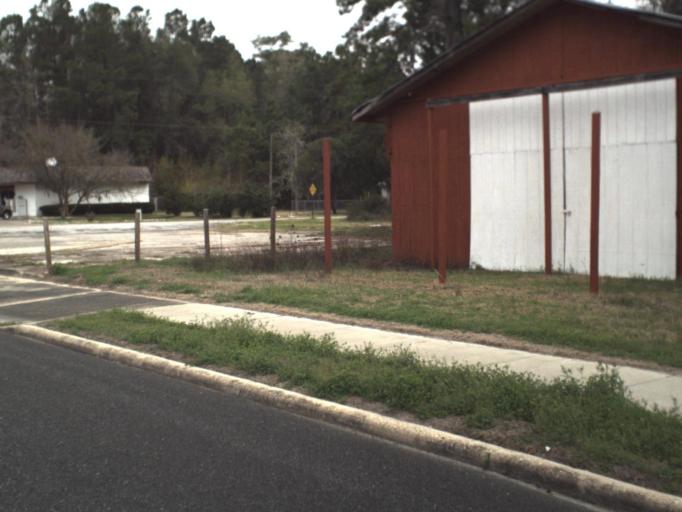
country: US
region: Florida
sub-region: Jefferson County
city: Monticello
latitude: 30.3769
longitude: -83.8124
